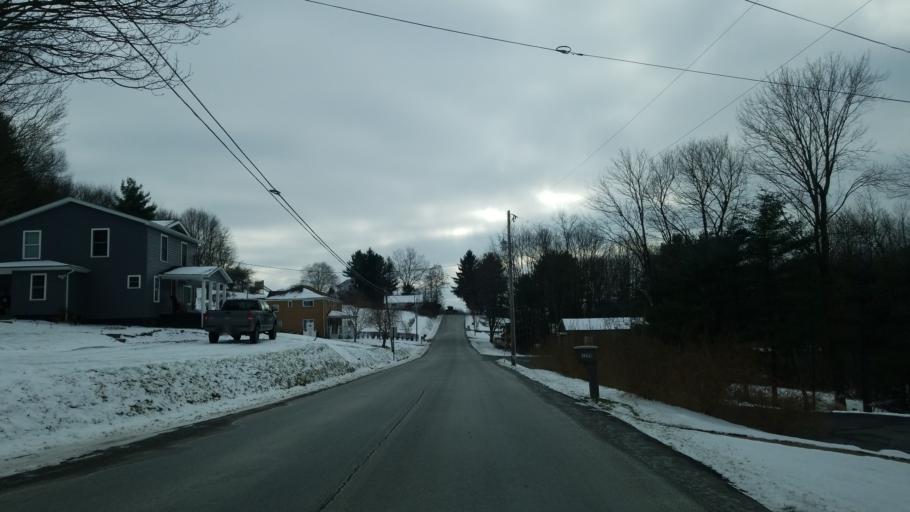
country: US
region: Pennsylvania
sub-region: Clearfield County
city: Sandy
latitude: 41.0836
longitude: -78.7492
